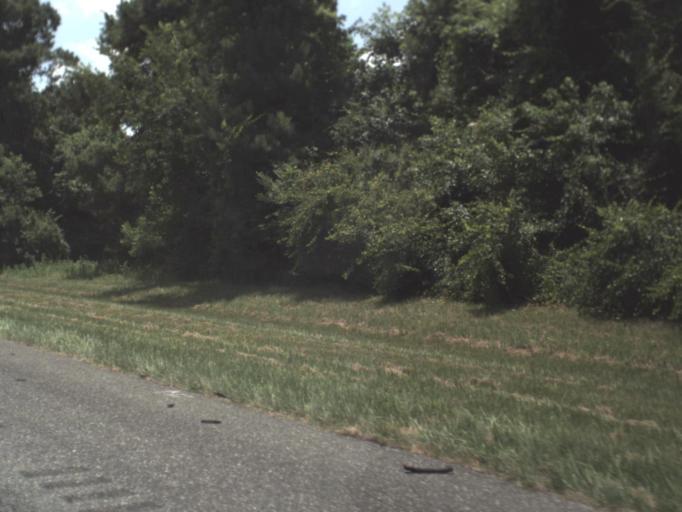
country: US
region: Florida
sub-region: Jefferson County
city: Monticello
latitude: 30.4439
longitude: -83.6744
